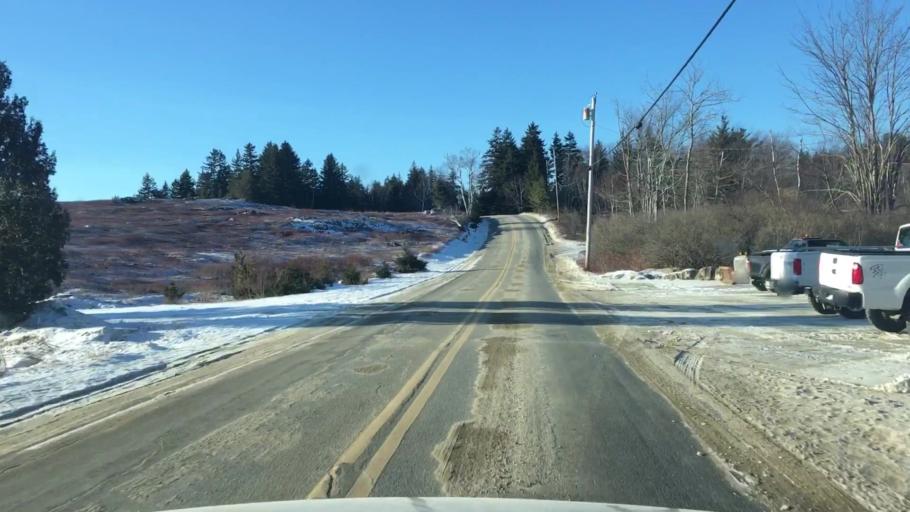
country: US
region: Maine
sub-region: Hancock County
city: Castine
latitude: 44.3652
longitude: -68.7508
